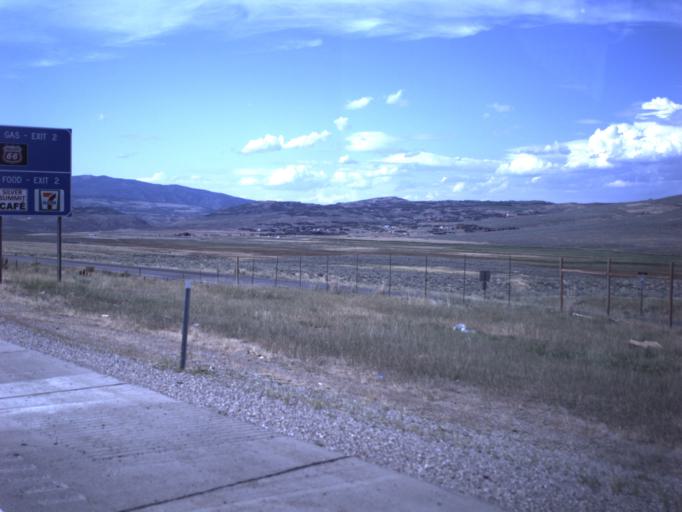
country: US
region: Utah
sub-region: Summit County
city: Park City
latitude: 40.6990
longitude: -111.4728
